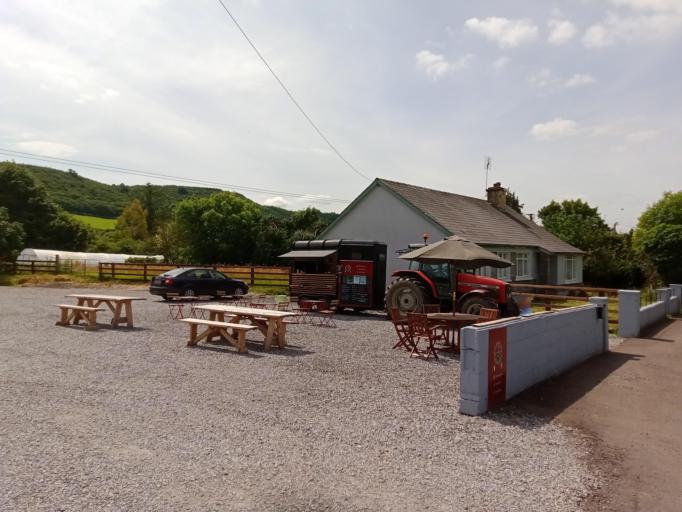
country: IE
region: Leinster
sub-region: Laois
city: Rathdowney
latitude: 52.8051
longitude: -7.4633
